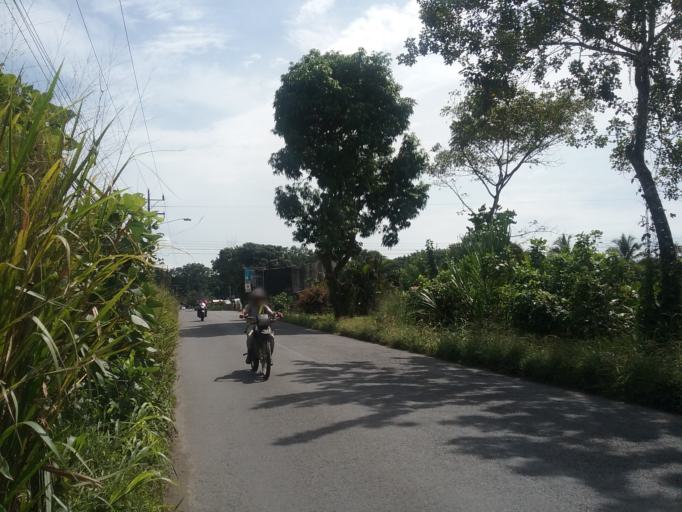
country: CR
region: Limon
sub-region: Canton de Pococi
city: Guapiles
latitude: 10.3204
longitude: -83.8955
